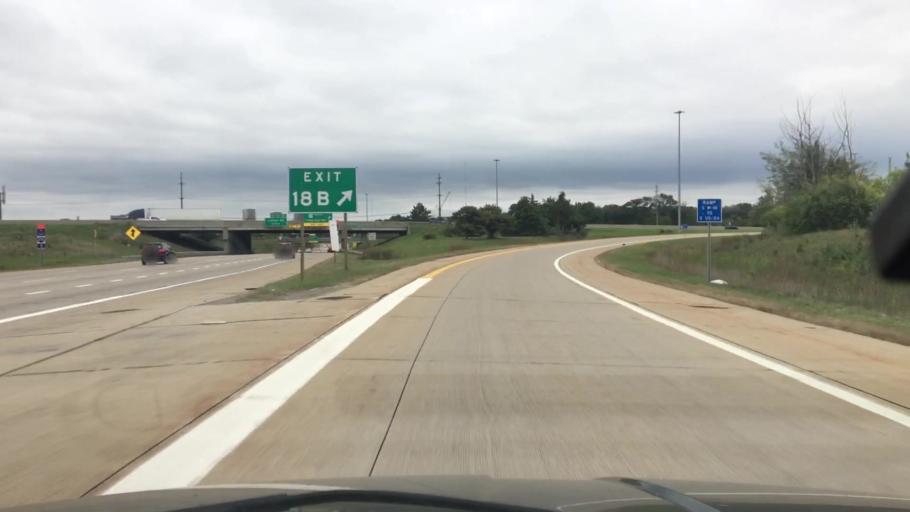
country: US
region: Michigan
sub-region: Oakland County
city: Bingham Farms
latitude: 42.4890
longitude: -83.2870
